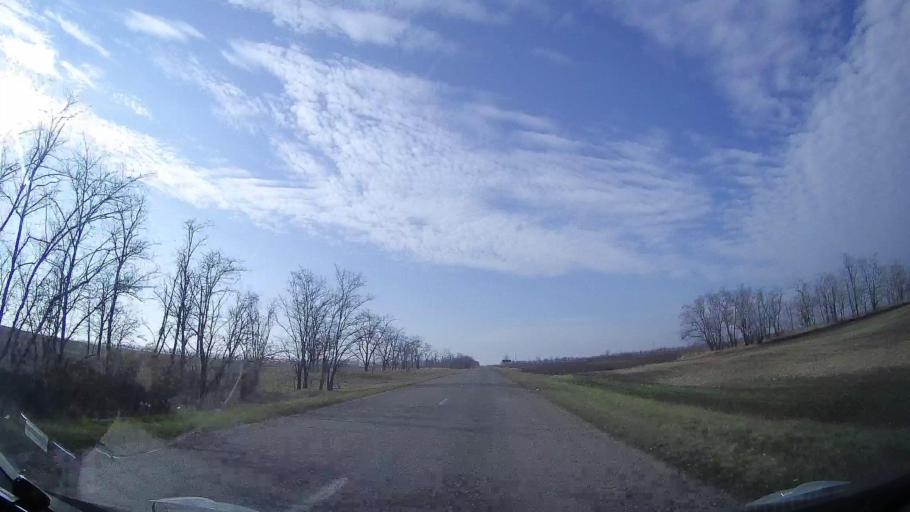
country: RU
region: Rostov
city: Gigant
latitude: 46.8487
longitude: 41.3071
